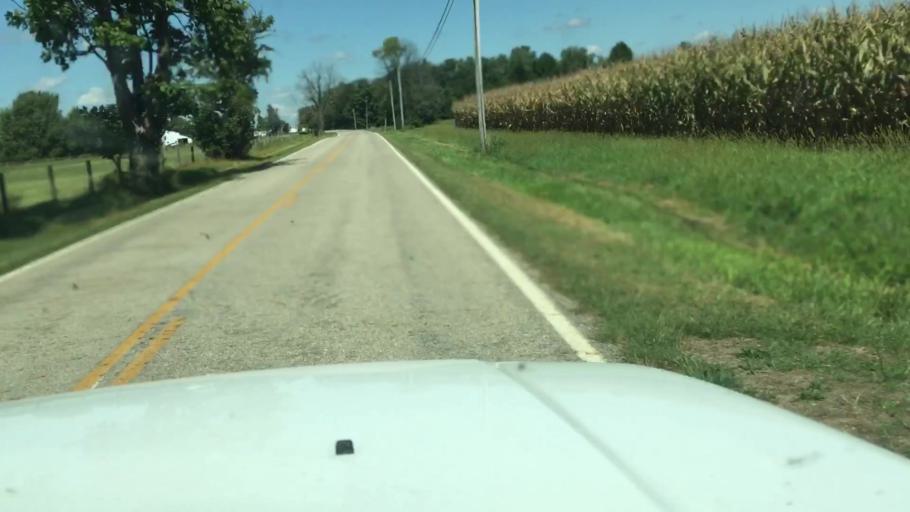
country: US
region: Ohio
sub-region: Madison County
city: Mount Sterling
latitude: 39.6825
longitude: -83.2363
